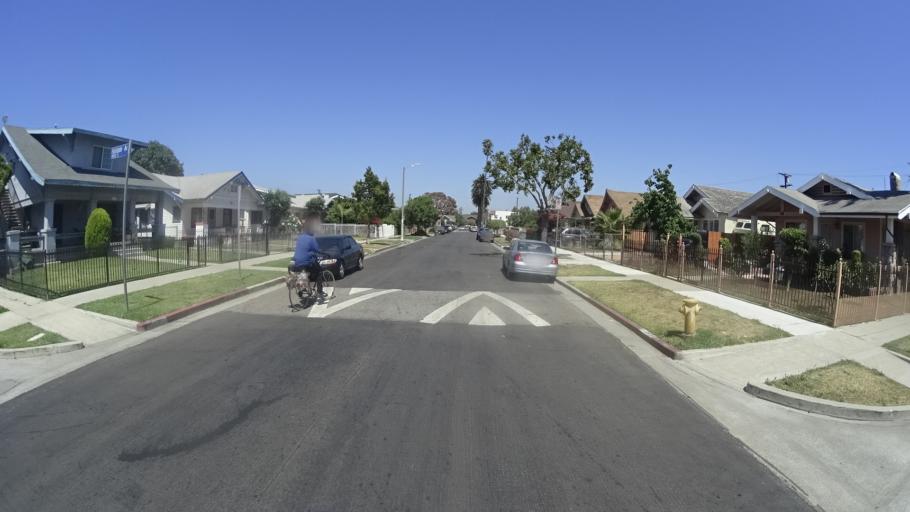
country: US
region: California
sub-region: Los Angeles County
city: View Park-Windsor Hills
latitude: 33.9982
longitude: -118.3023
